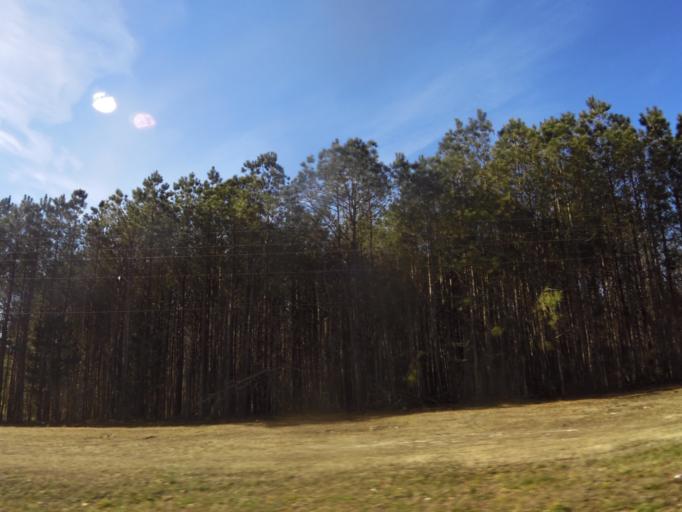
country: US
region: Virginia
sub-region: Isle of Wight County
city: Isle of Wight
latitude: 36.9411
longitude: -76.6871
